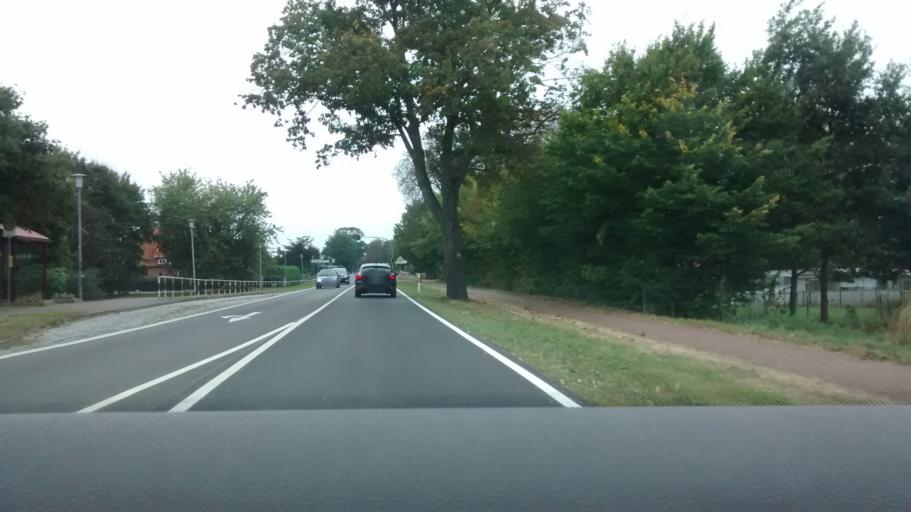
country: DE
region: Mecklenburg-Vorpommern
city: Mecklenburg
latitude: 53.8167
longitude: 11.4469
